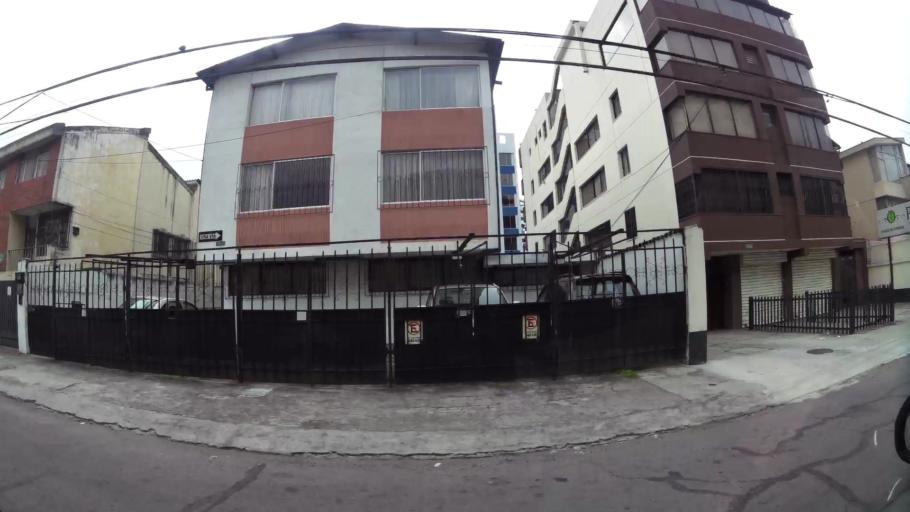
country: EC
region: Pichincha
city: Quito
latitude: -0.1904
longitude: -78.4889
